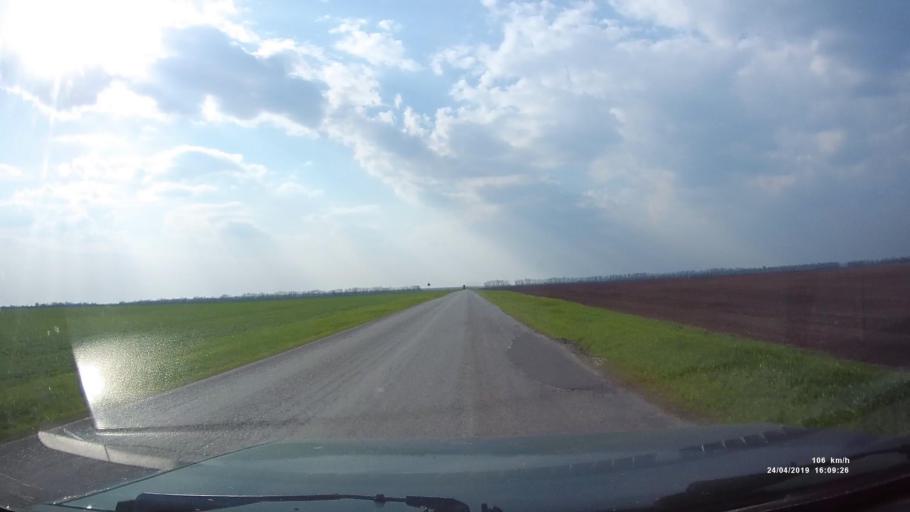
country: RU
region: Rostov
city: Sovetskoye
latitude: 46.7080
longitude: 42.2897
